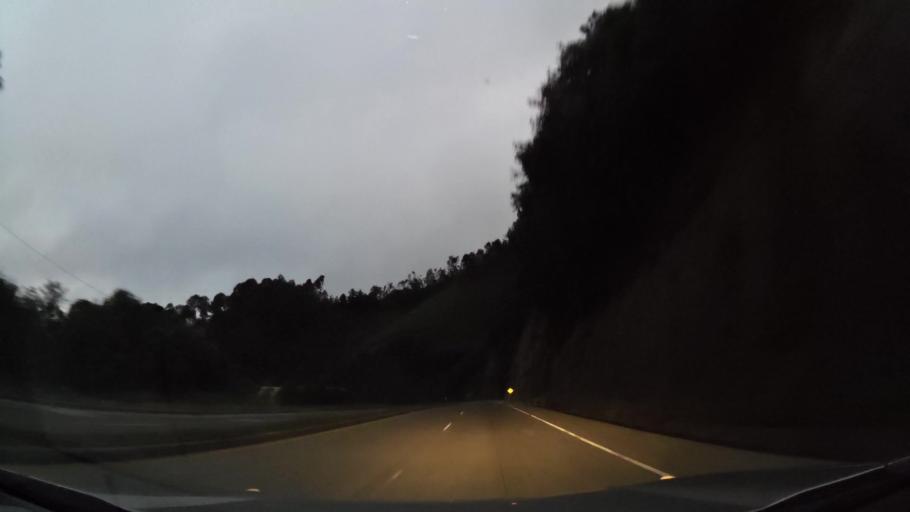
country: GT
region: Chimaltenango
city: Santa Apolonia
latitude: 14.8190
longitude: -91.0048
